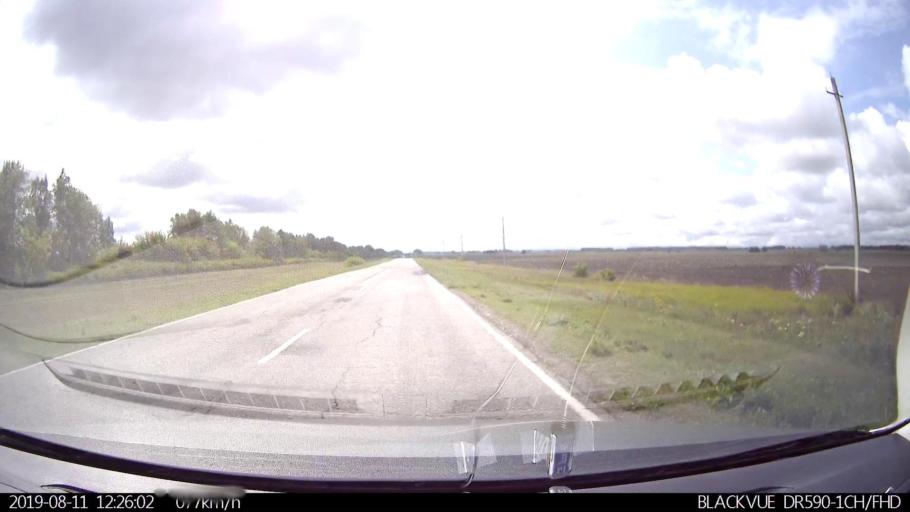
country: RU
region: Ulyanovsk
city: Ignatovka
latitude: 53.8680
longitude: 47.9341
